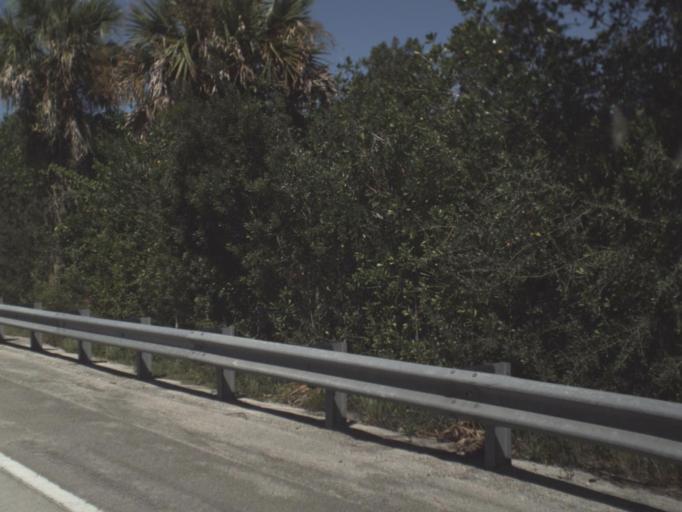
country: US
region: Florida
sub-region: Collier County
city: Marco
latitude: 25.9633
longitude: -81.5228
